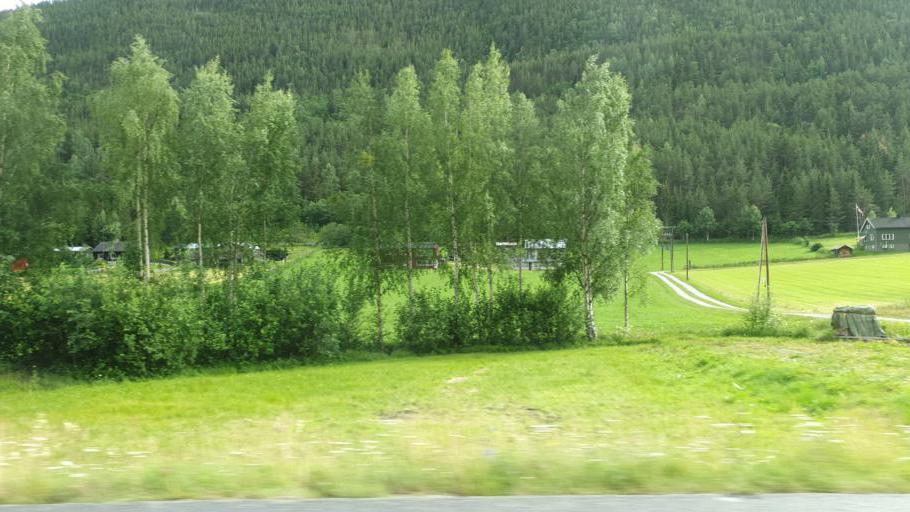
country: NO
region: Oppland
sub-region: Dovre
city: Dovre
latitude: 61.8443
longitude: 9.3681
